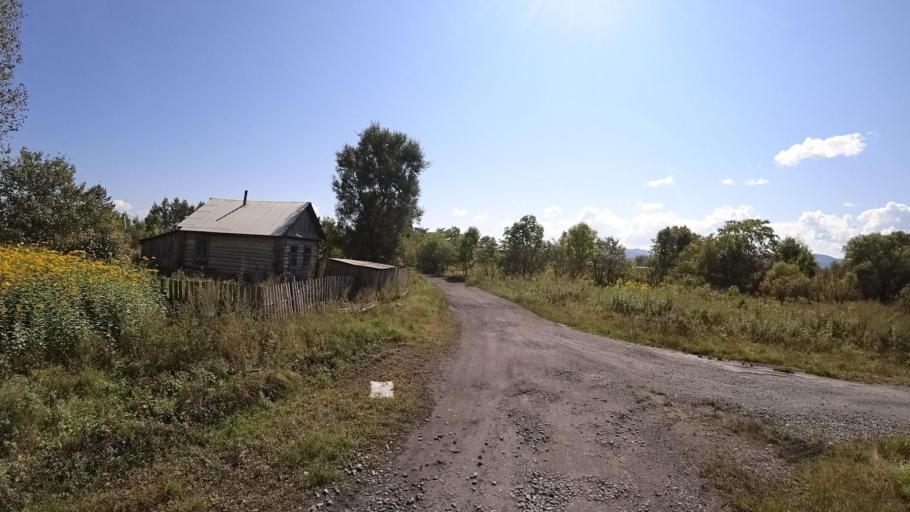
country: RU
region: Jewish Autonomous Oblast
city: Londoko
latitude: 49.0046
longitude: 131.9434
